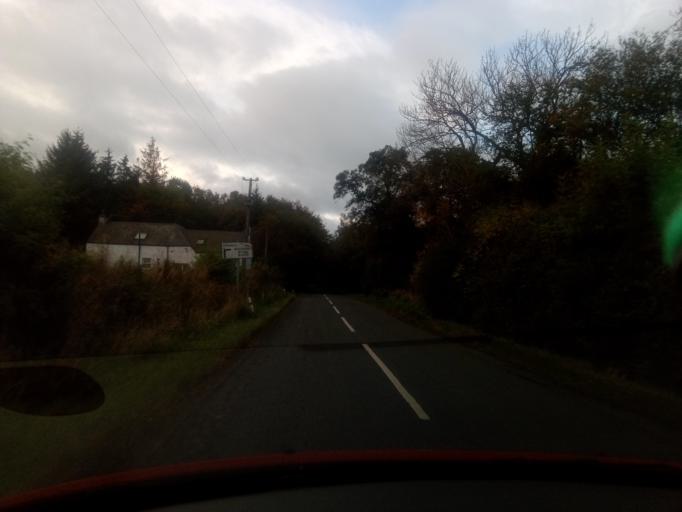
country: GB
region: Scotland
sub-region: The Scottish Borders
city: Jedburgh
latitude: 55.4231
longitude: -2.6166
